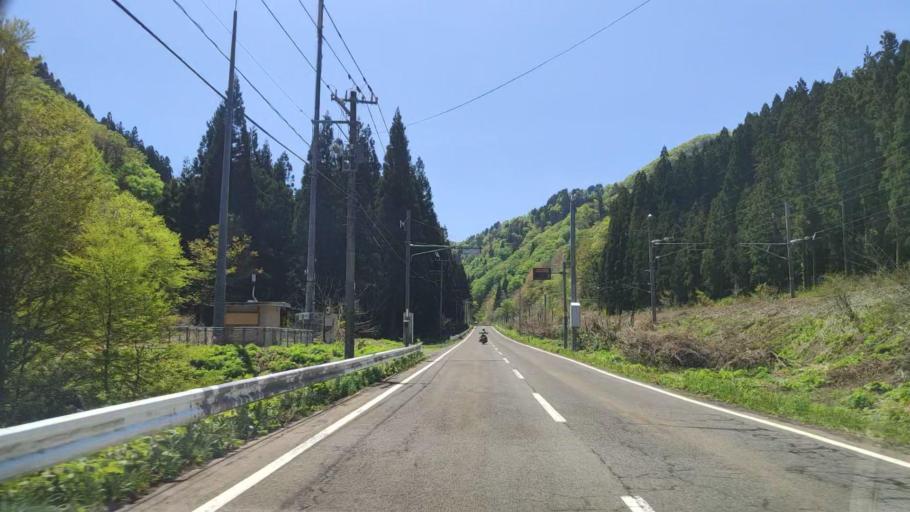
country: JP
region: Akita
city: Yuzawa
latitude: 39.0208
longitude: 140.3757
